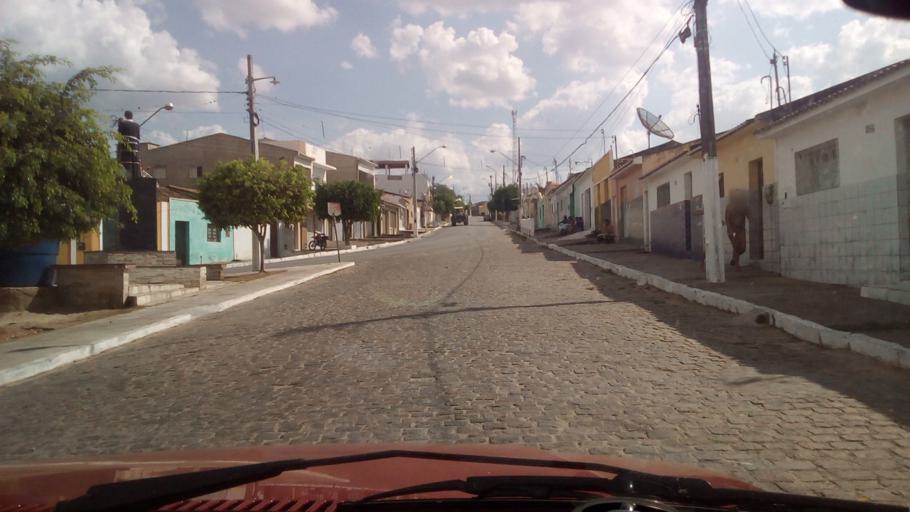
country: BR
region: Paraiba
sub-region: Arara
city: Arara
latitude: -6.8257
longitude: -35.7605
